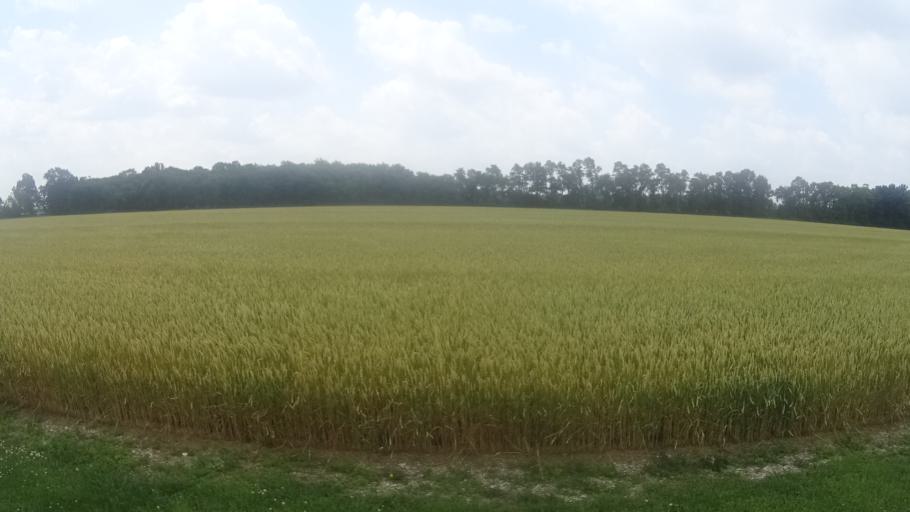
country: US
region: Ohio
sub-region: Huron County
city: Monroeville
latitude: 41.3073
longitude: -82.7075
